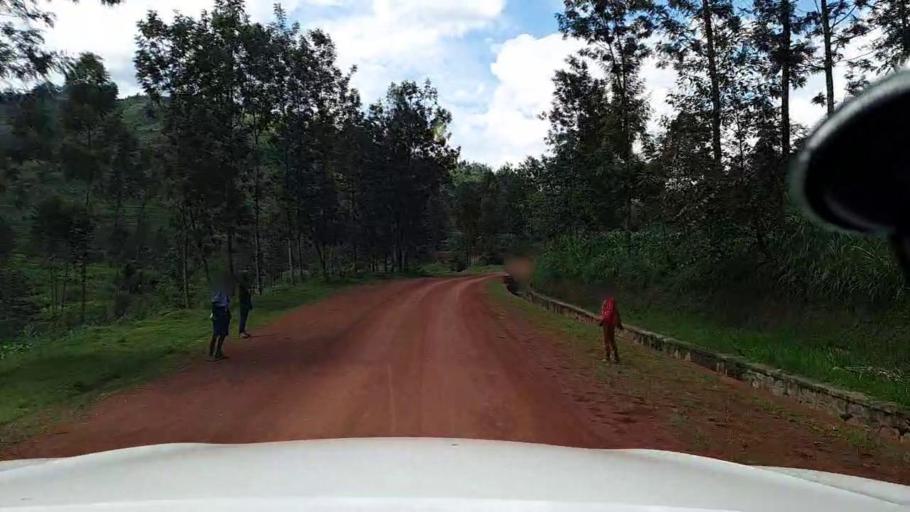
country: RW
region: Northern Province
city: Byumba
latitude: -1.7055
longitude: 29.8423
